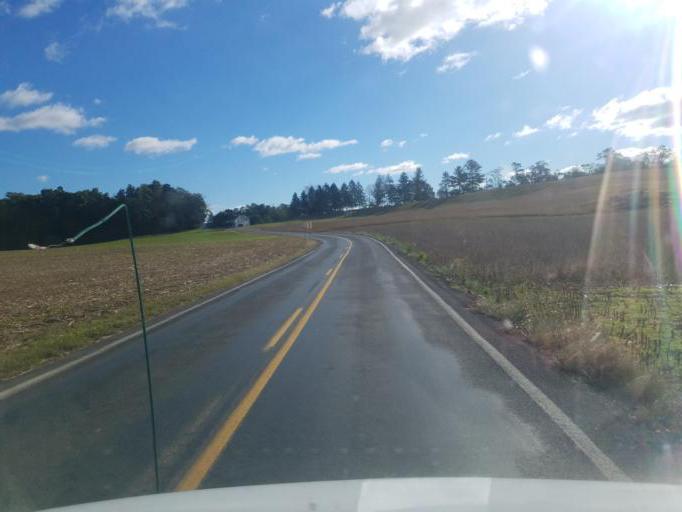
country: US
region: Pennsylvania
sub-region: Franklin County
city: Guilford Siding
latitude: 39.8093
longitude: -77.6411
